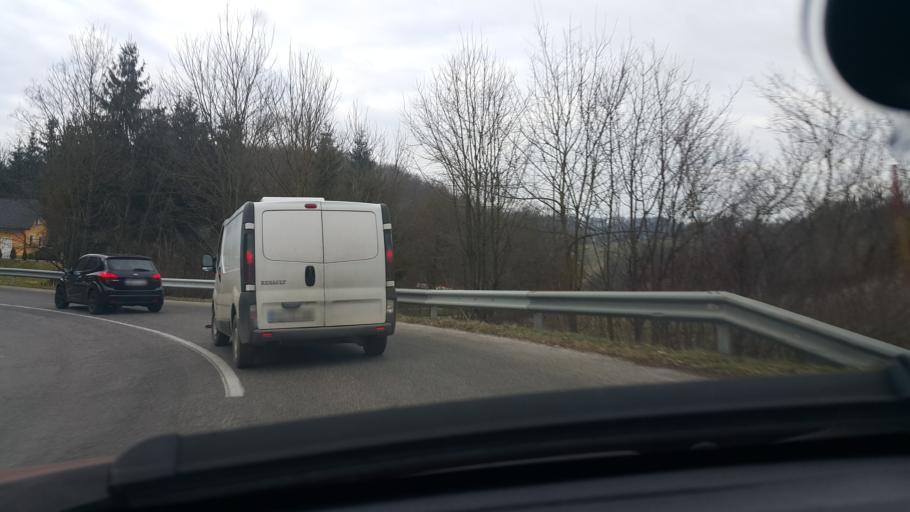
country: SI
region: Bistrica ob Sotli
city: Bistrica ob Sotli
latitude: 46.0772
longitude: 15.6316
